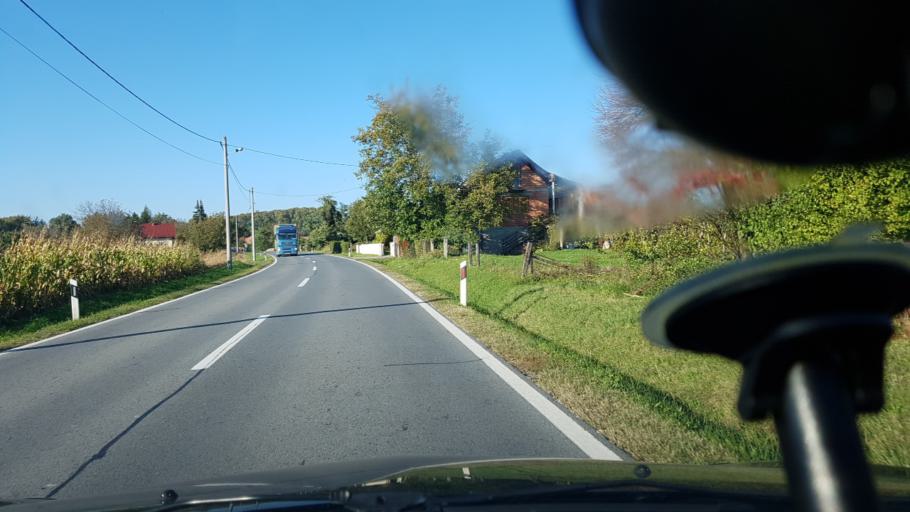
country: HR
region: Bjelovarsko-Bilogorska
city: Bjelovar
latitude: 45.9758
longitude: 16.8955
